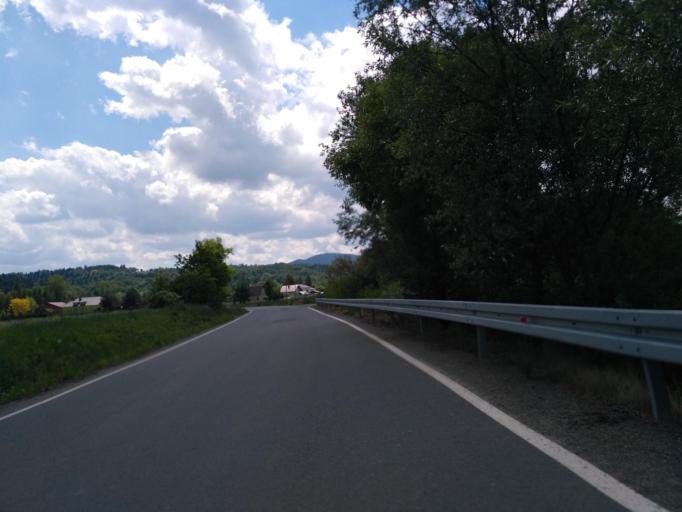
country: PL
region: Subcarpathian Voivodeship
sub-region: Powiat krosnienski
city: Dukla
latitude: 49.5810
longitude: 21.6939
